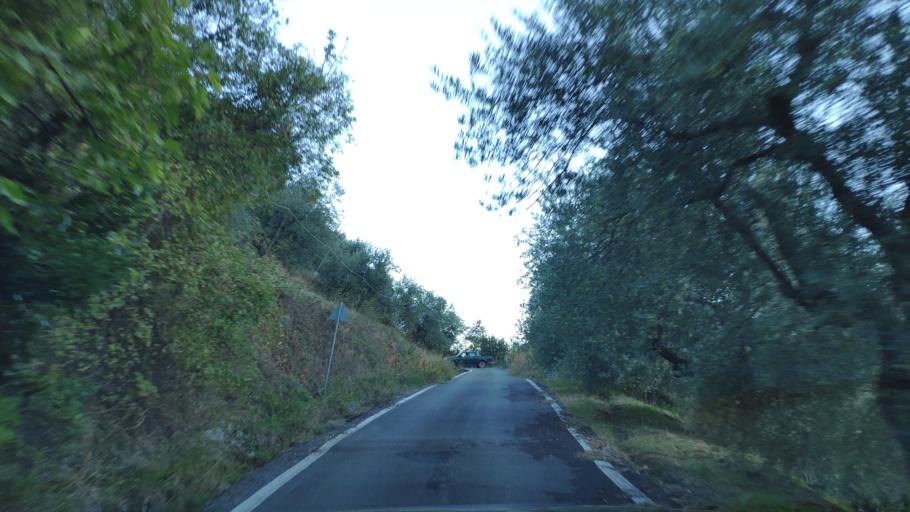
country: GR
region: Peloponnese
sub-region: Nomos Arkadias
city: Dimitsana
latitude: 37.5676
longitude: 22.0454
